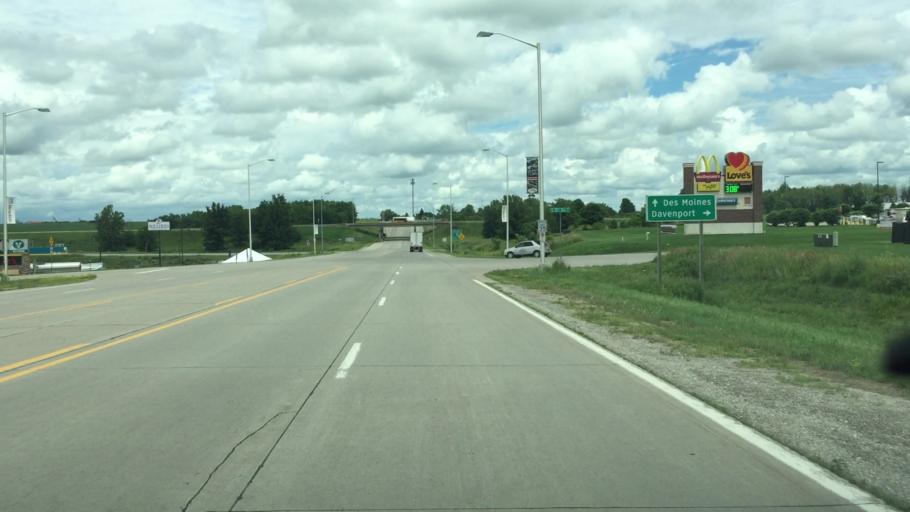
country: US
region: Iowa
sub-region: Jasper County
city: Newton
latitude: 41.6789
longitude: -92.9998
